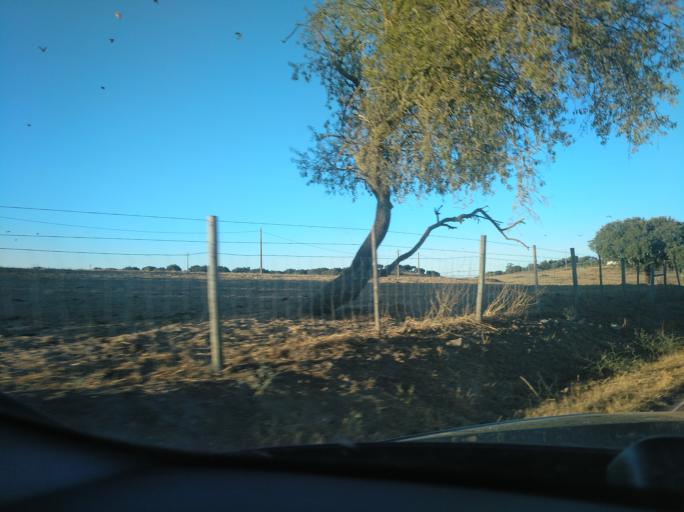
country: PT
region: Portalegre
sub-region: Arronches
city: Arronches
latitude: 39.0677
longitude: -7.2663
